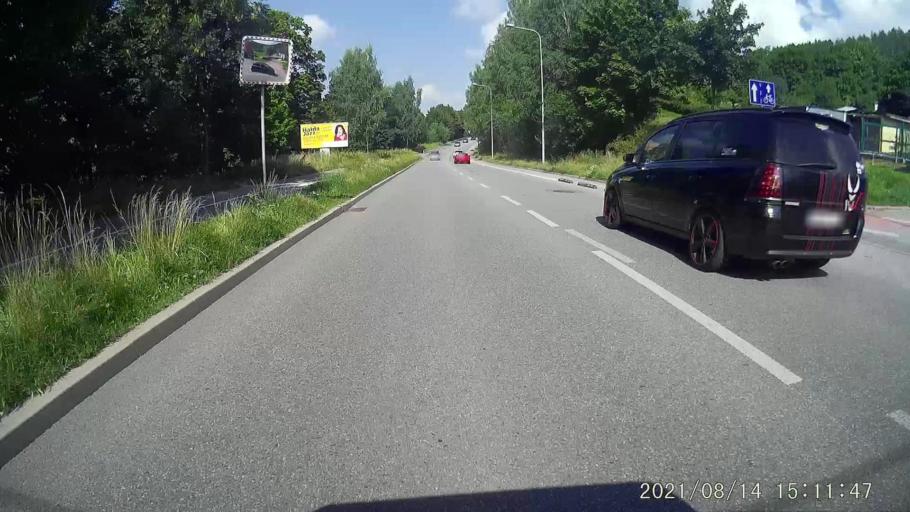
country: PL
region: Lower Silesian Voivodeship
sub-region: Powiat walbrzyski
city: Walbrzych
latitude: 50.7536
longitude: 16.3135
